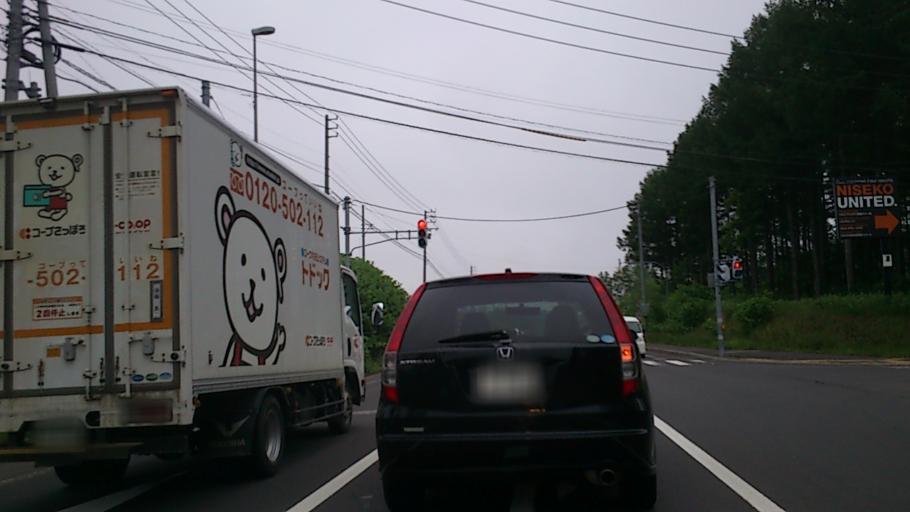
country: JP
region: Hokkaido
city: Niseko Town
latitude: 42.8633
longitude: 140.7454
